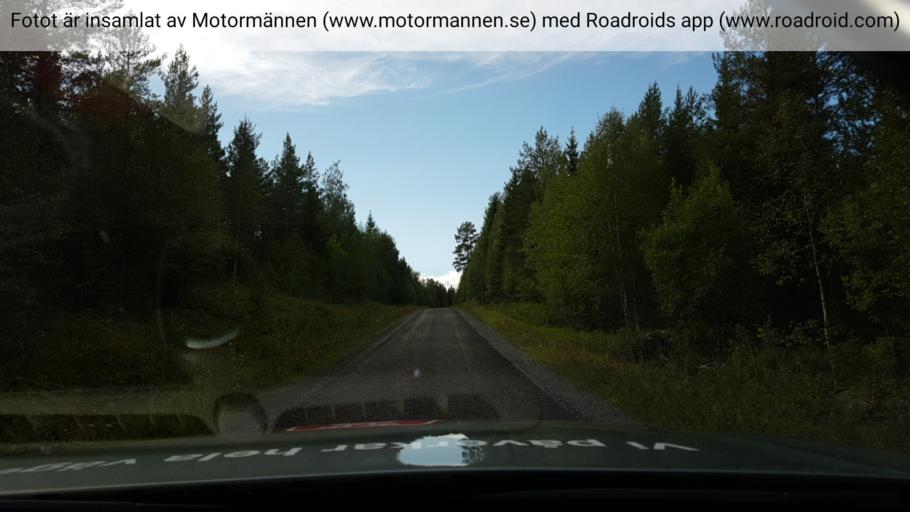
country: SE
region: Jaemtland
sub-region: OEstersunds Kommun
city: Lit
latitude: 63.3009
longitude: 15.3108
